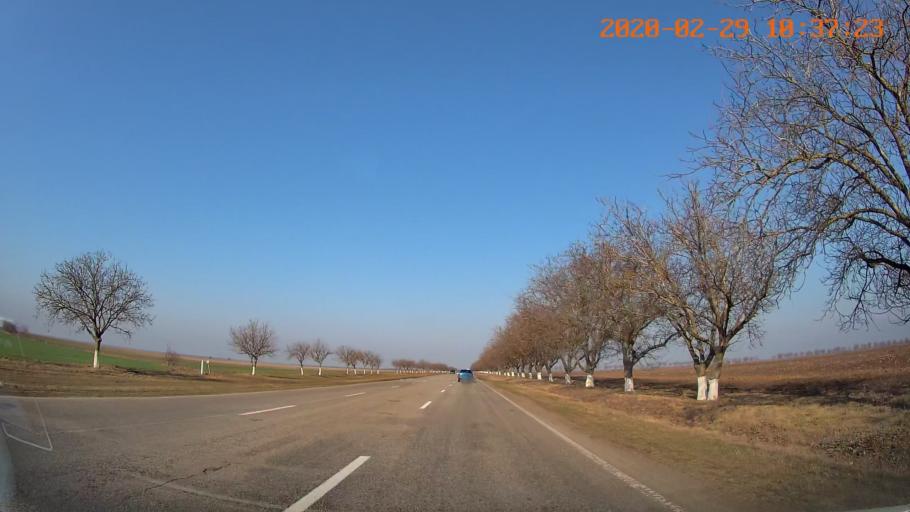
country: MD
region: Anenii Noi
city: Varnita
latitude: 47.0053
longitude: 29.4906
